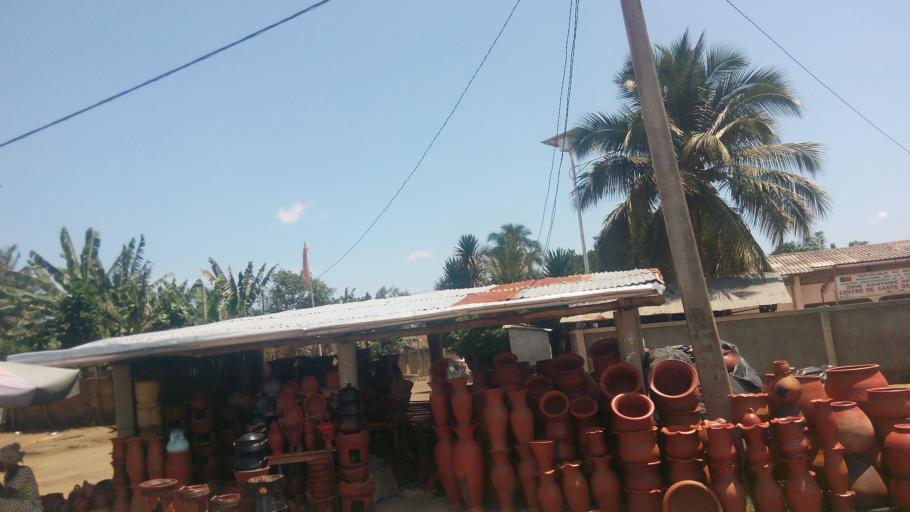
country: BJ
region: Mono
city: Come
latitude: 6.4021
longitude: 1.9081
